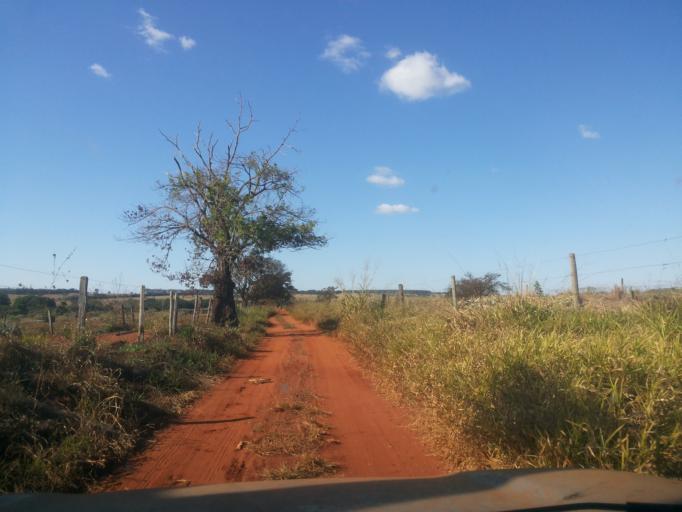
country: BR
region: Minas Gerais
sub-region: Centralina
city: Centralina
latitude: -18.7380
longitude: -49.1827
